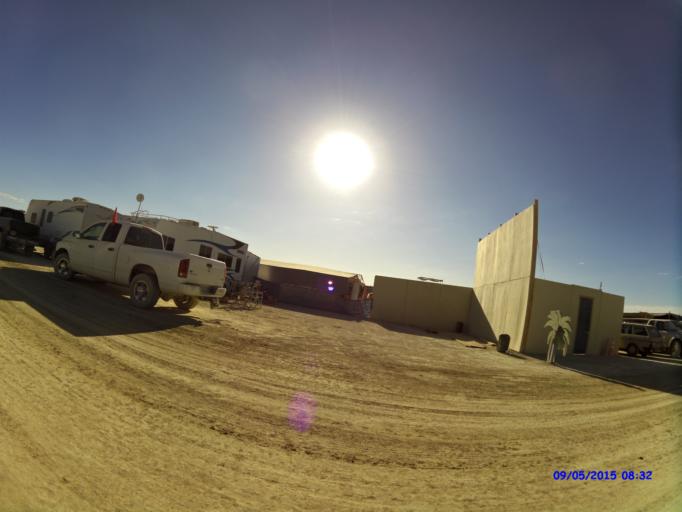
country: US
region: Nevada
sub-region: Pershing County
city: Lovelock
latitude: 40.7814
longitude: -119.2165
